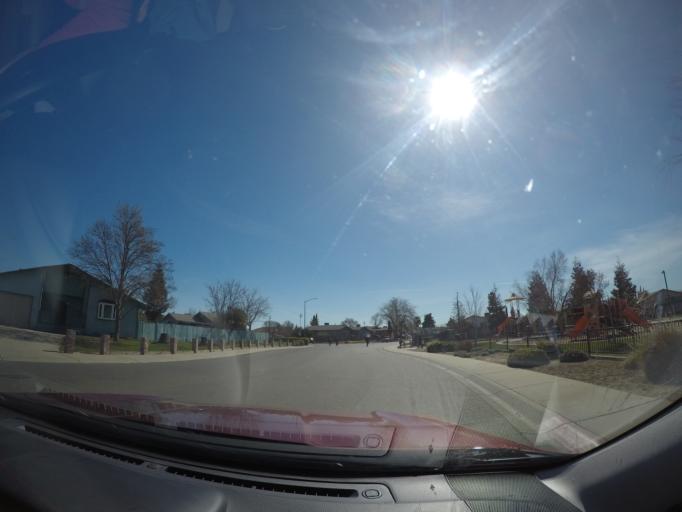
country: US
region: California
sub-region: Colusa County
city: Williams
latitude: 39.1594
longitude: -122.1610
